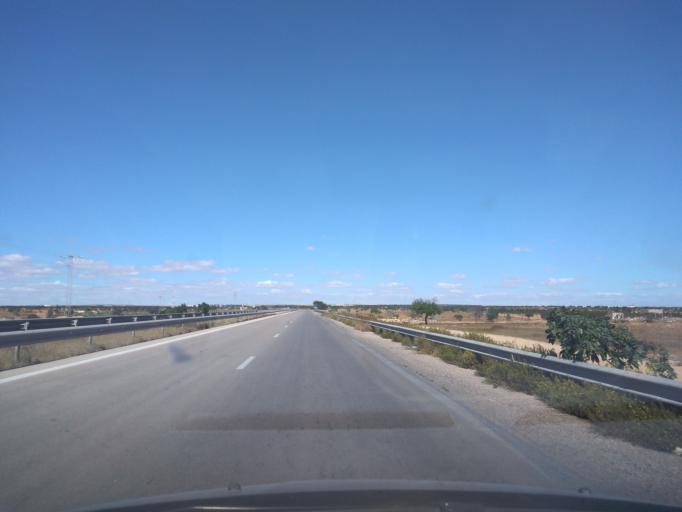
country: TN
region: Safaqis
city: Al Qarmadah
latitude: 34.8760
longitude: 10.7363
